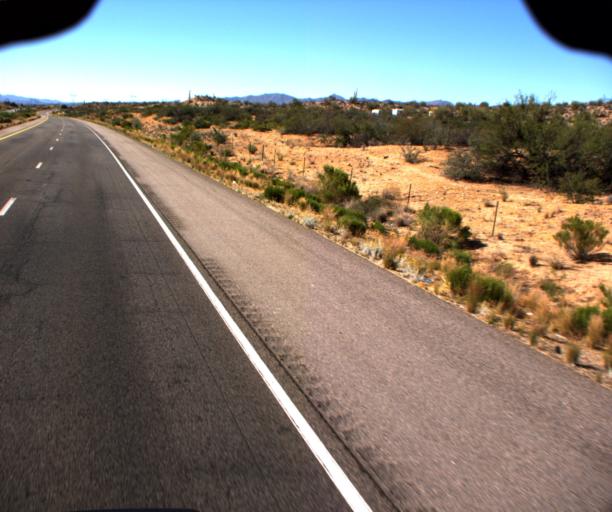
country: US
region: Arizona
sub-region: Yavapai County
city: Bagdad
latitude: 34.7651
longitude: -113.6190
